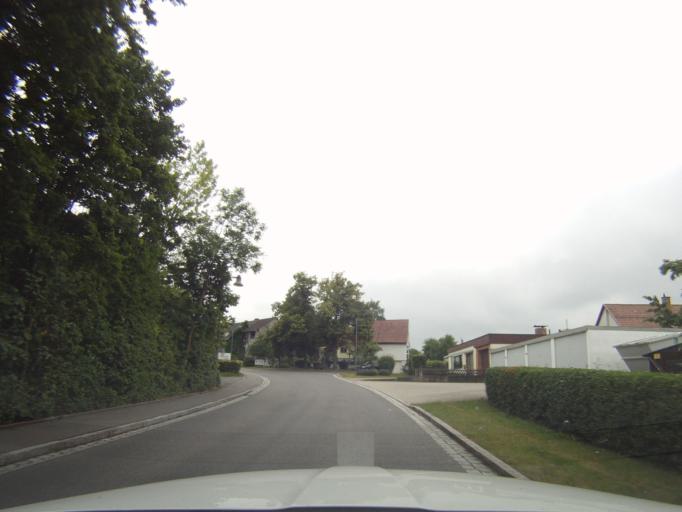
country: DE
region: Bavaria
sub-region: Upper Franconia
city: Ahorn
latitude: 50.2393
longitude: 10.9569
